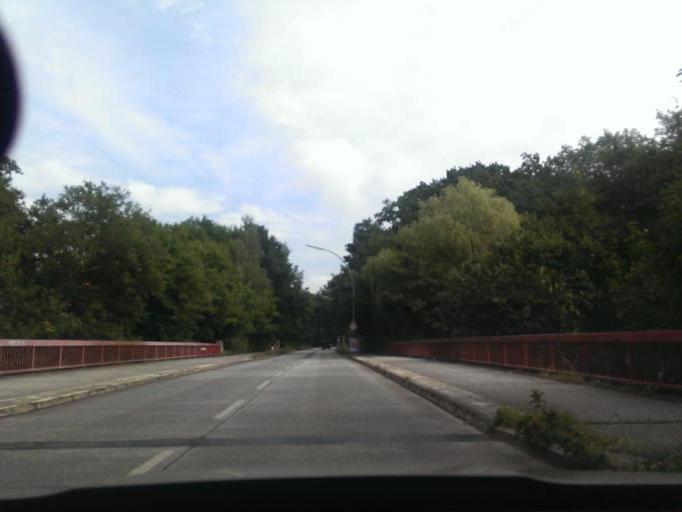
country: DE
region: Hamburg
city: Poppenbuettel
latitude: 53.6708
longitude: 10.0873
